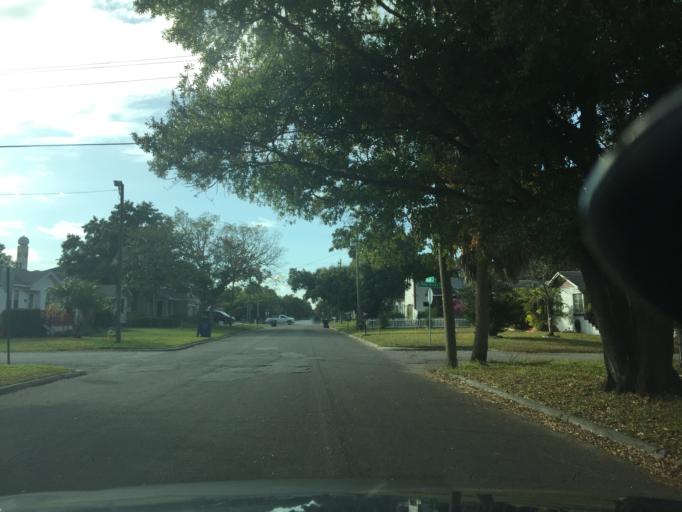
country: US
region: Florida
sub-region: Hillsborough County
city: Tampa
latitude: 27.9472
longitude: -82.4920
